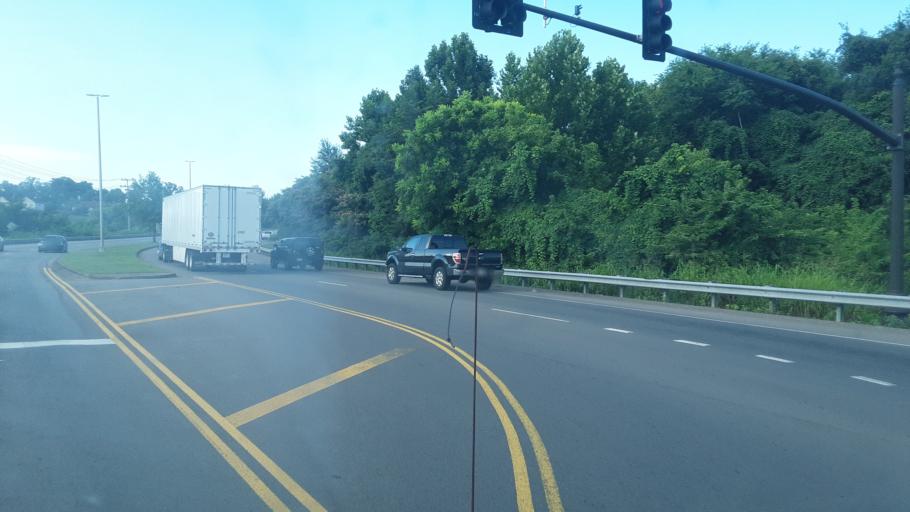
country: US
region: Tennessee
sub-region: Montgomery County
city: Clarksville
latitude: 36.5804
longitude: -87.2780
